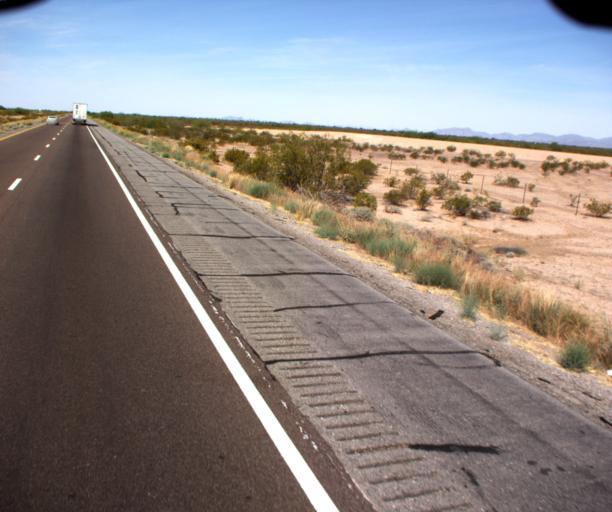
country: US
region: Arizona
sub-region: La Paz County
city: Salome
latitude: 33.5465
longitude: -113.2033
